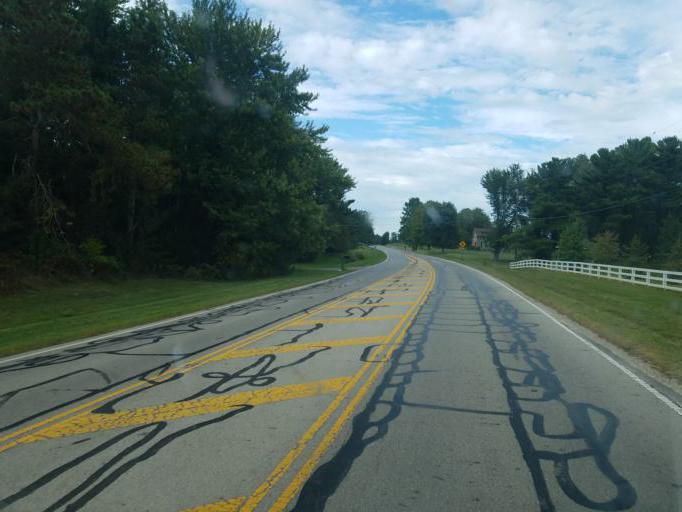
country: US
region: Ohio
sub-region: Delaware County
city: Sunbury
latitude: 40.2305
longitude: -82.7898
